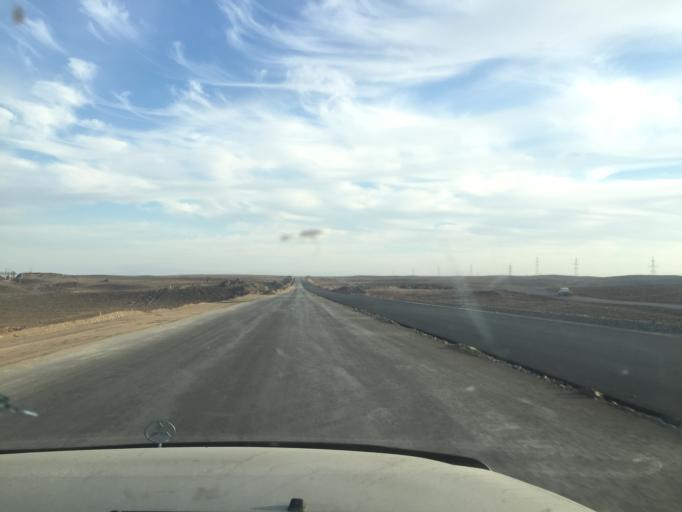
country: KZ
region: Zhambyl
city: Mynaral
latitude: 45.2760
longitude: 73.7834
